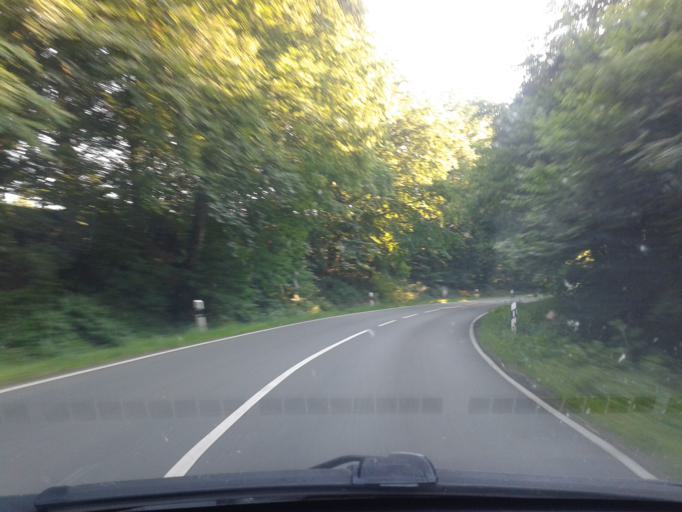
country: DE
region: North Rhine-Westphalia
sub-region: Regierungsbezirk Detmold
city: Lemgo
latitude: 51.9985
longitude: 8.9186
